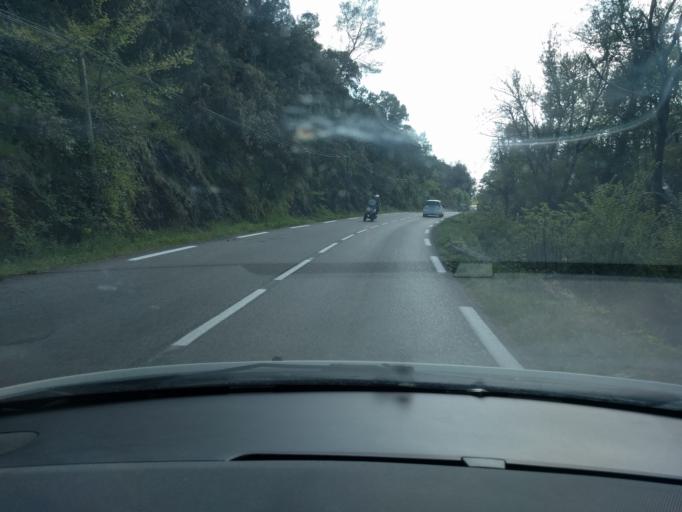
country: FR
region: Provence-Alpes-Cote d'Azur
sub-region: Departement du Var
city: Pierrefeu-du-Var
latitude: 43.2092
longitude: 6.1399
